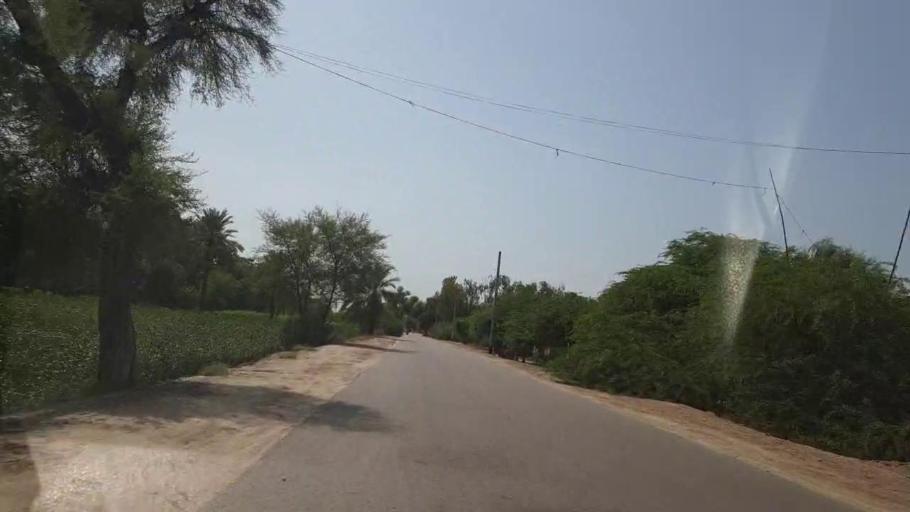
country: PK
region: Sindh
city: Bozdar
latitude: 27.1216
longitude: 68.5471
